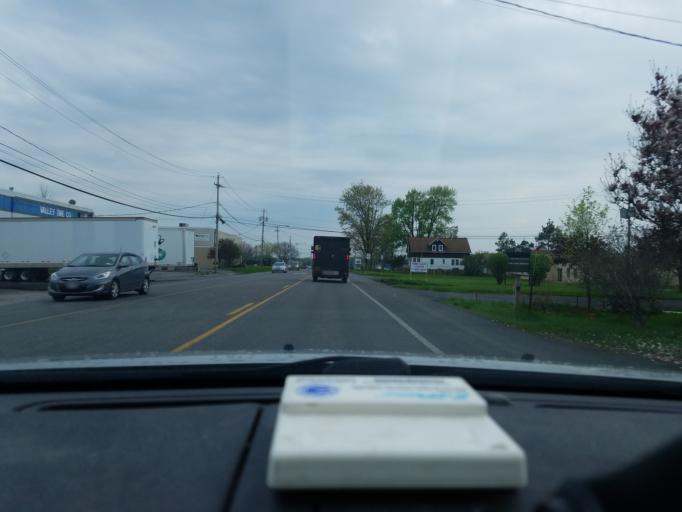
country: US
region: New York
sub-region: Onondaga County
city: East Syracuse
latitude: 43.0999
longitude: -76.0843
